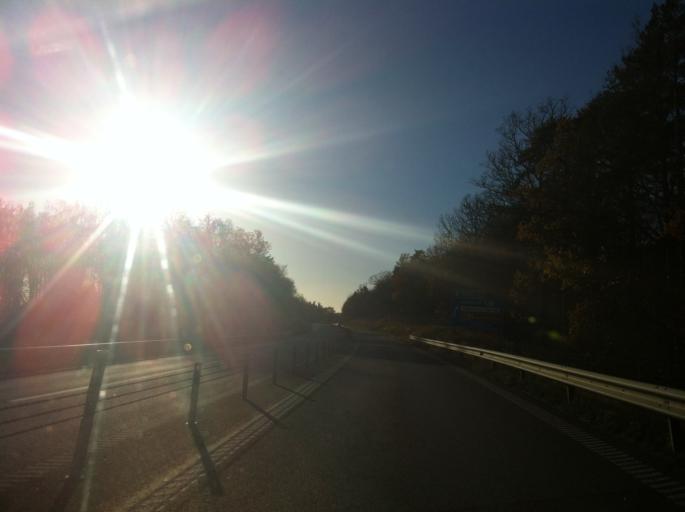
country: SE
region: Blekinge
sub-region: Karlshamns Kommun
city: Morrum
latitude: 56.1886
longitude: 14.7875
